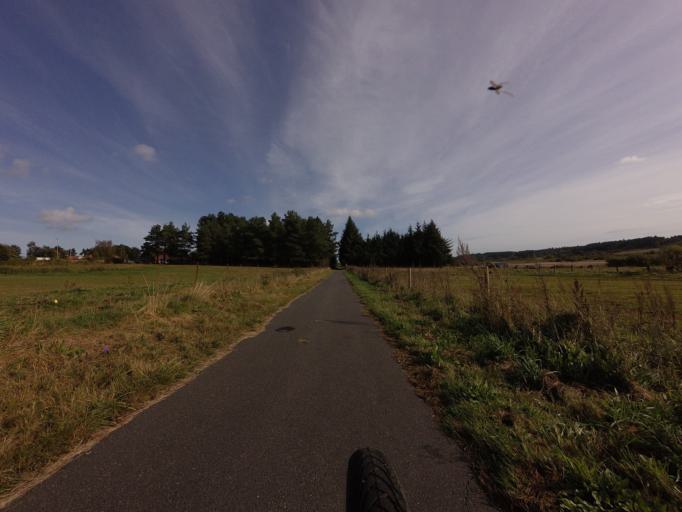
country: DK
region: Central Jutland
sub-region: Viborg Kommune
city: Bjerringbro
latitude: 56.4414
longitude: 9.5614
